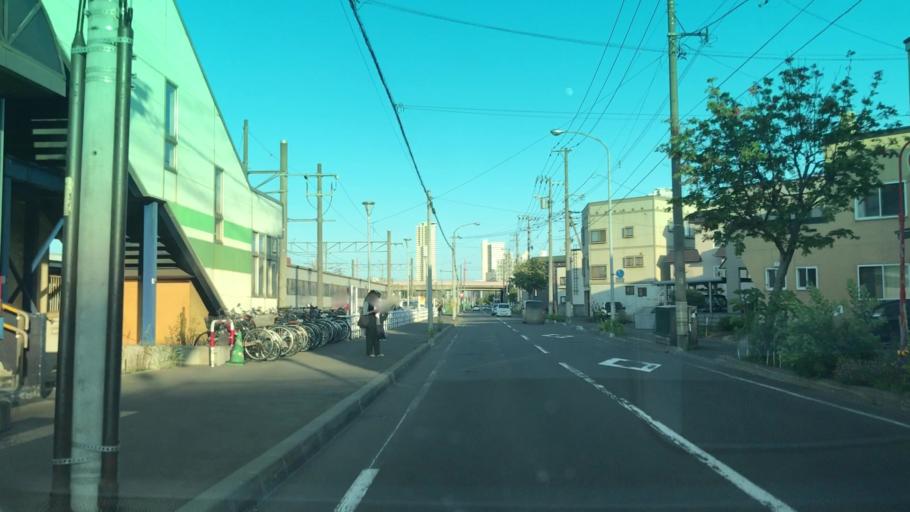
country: JP
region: Hokkaido
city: Sapporo
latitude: 43.0895
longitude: 141.2938
